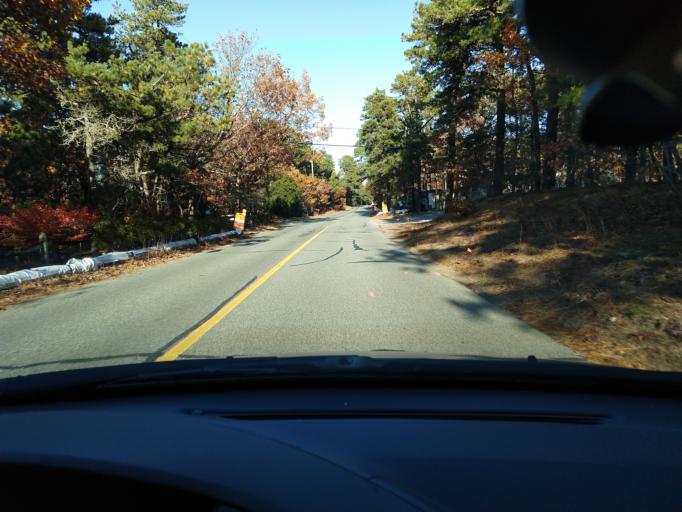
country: US
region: Massachusetts
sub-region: Barnstable County
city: Eastham
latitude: 41.8185
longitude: -69.9867
